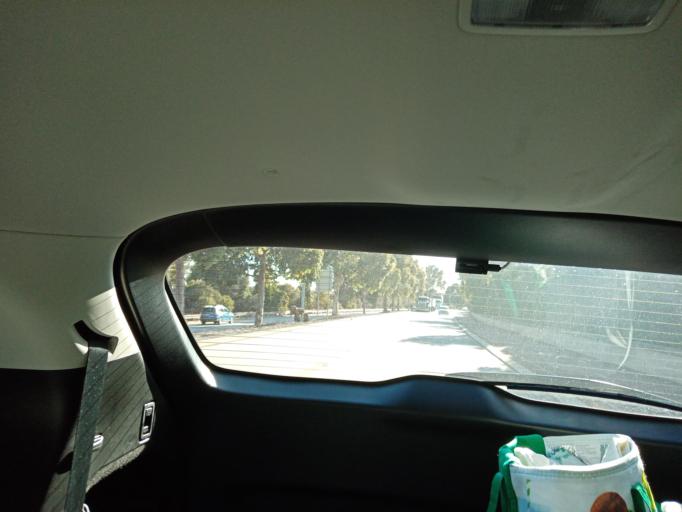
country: AU
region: Western Australia
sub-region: City of Cockburn
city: Yangebup
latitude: -32.1277
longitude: 115.8144
